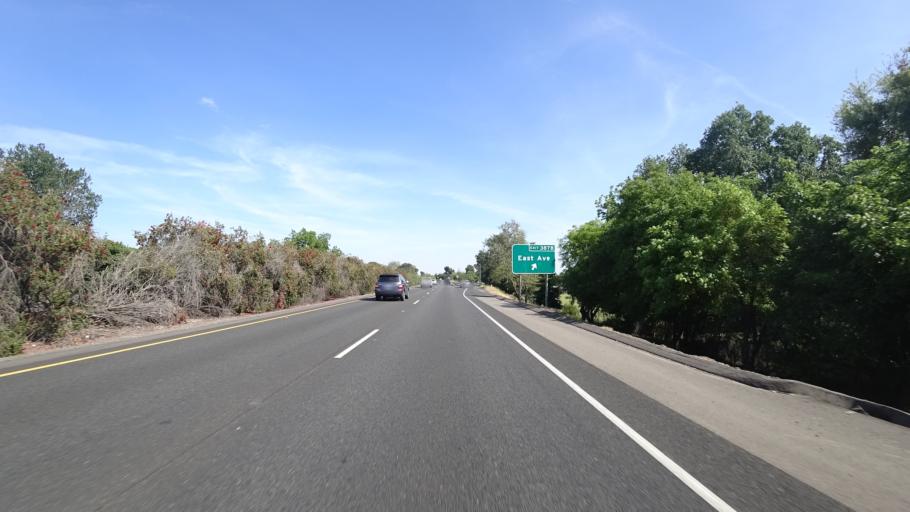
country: US
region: California
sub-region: Butte County
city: Chico
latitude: 39.7628
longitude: -121.8591
